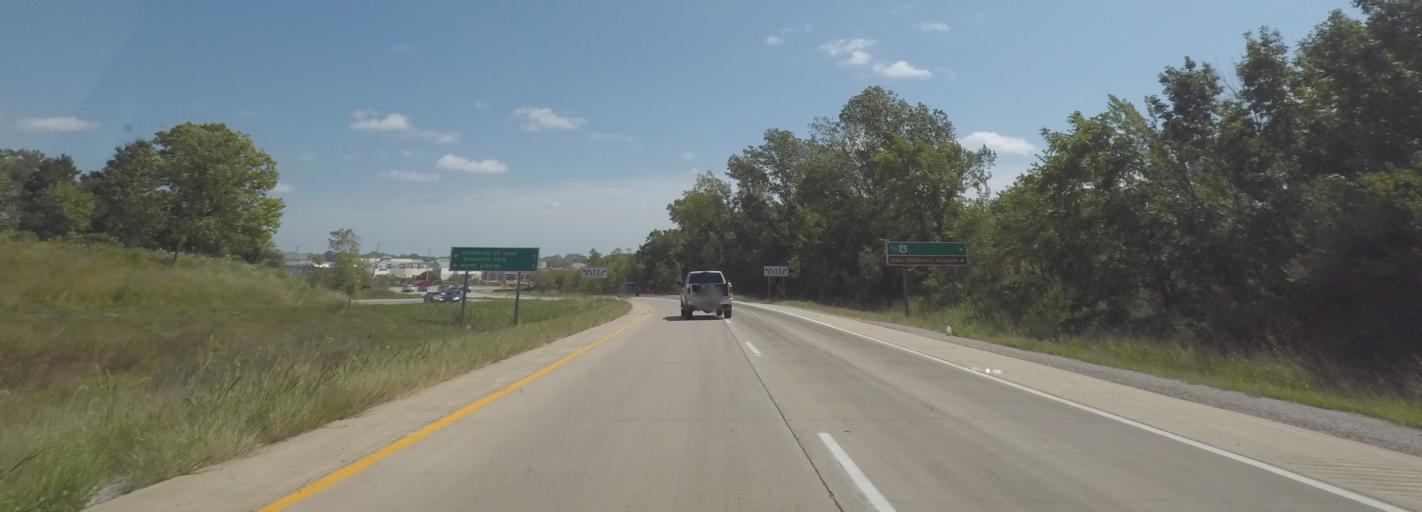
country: US
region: Iowa
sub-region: Johnson County
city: Coralville
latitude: 41.6927
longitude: -91.6114
